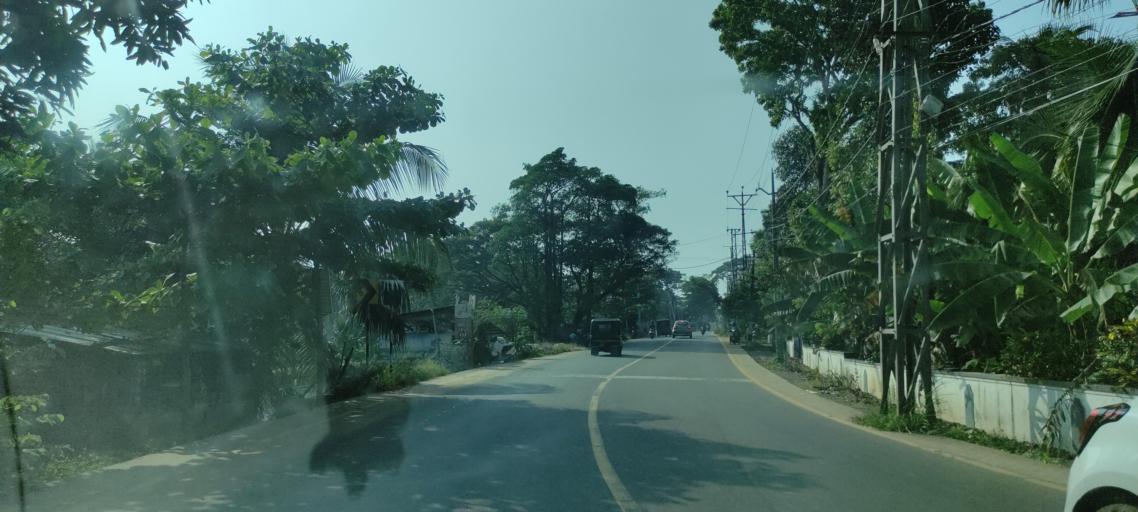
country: IN
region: Kerala
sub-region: Kottayam
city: Changanacheri
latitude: 9.3613
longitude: 76.4724
